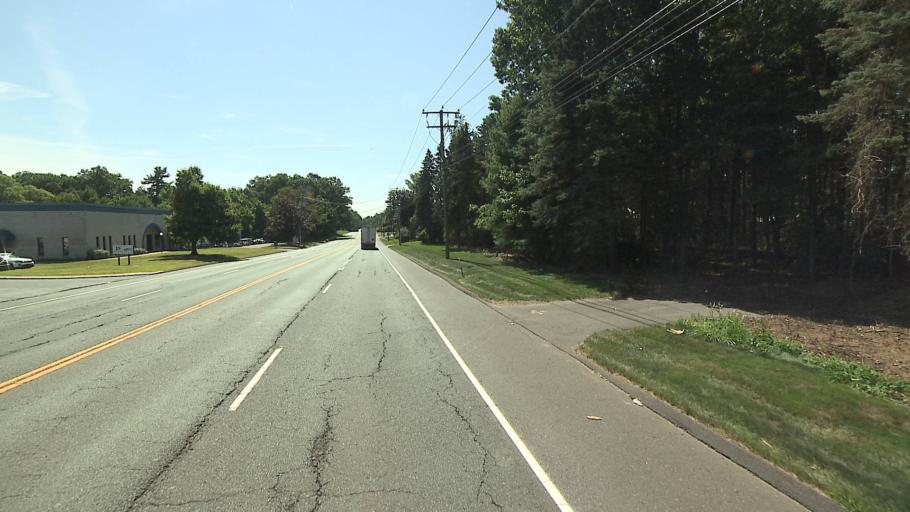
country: US
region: Connecticut
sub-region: Hartford County
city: Blue Hills
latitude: 41.8607
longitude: -72.7124
